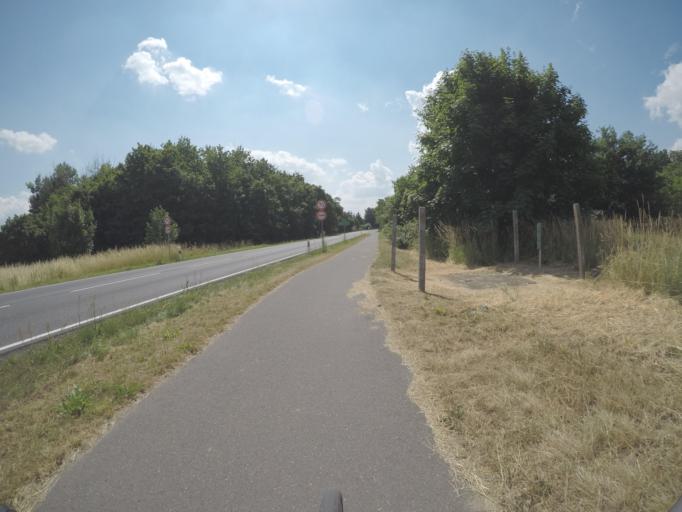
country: DE
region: Brandenburg
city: Wustermark
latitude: 52.5244
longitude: 12.9346
